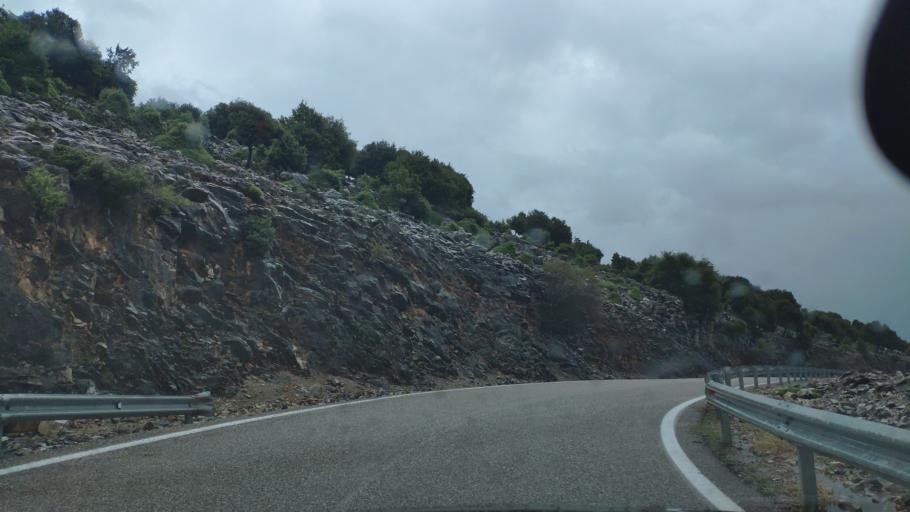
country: GR
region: Central Greece
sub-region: Nomos Evrytanias
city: Kerasochori
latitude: 39.0803
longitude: 21.3981
